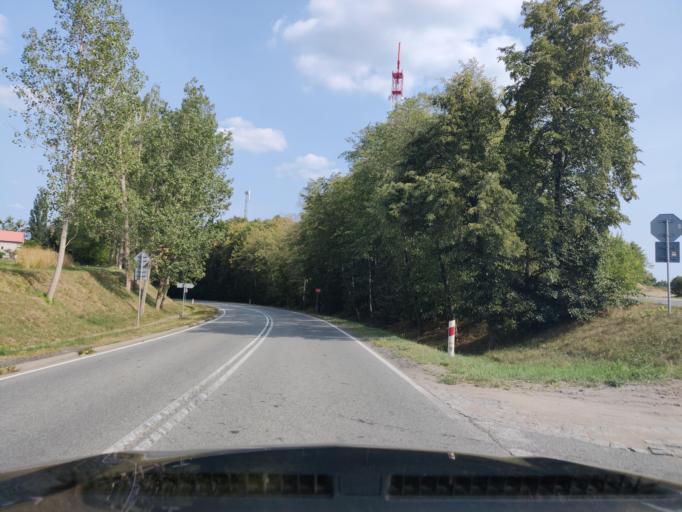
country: PL
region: Masovian Voivodeship
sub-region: Powiat makowski
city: Rozan
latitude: 52.8847
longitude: 21.3979
